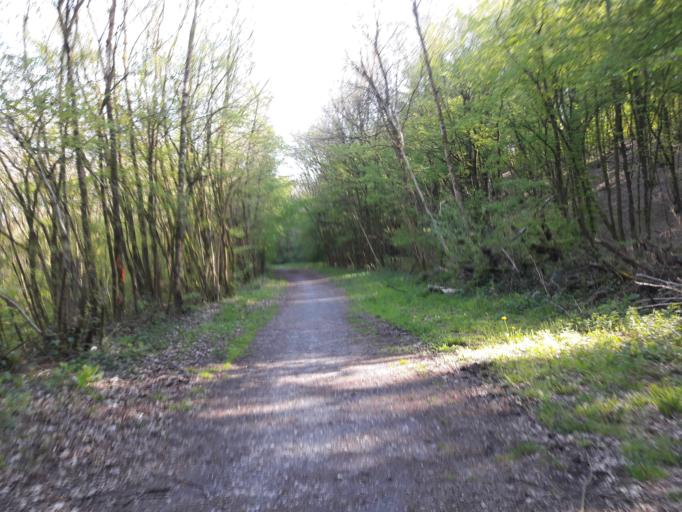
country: FR
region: Nord-Pas-de-Calais
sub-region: Departement du Nord
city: Sains-du-Nord
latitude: 50.1273
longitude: 4.0656
